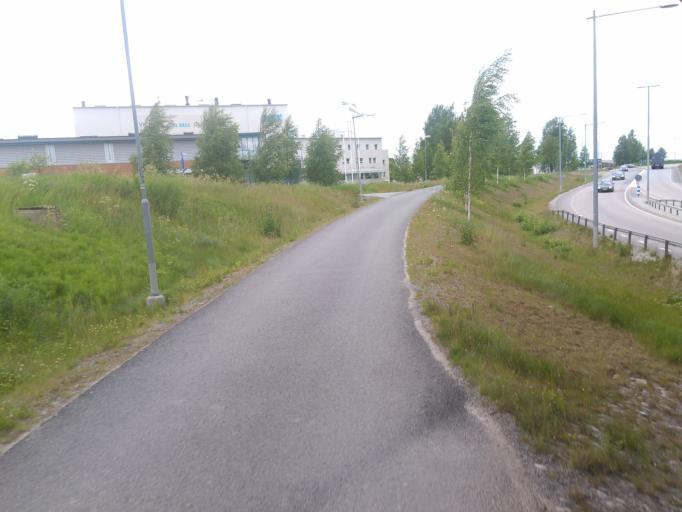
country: SE
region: Vaesterbotten
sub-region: Umea Kommun
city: Umea
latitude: 63.8398
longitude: 20.2441
